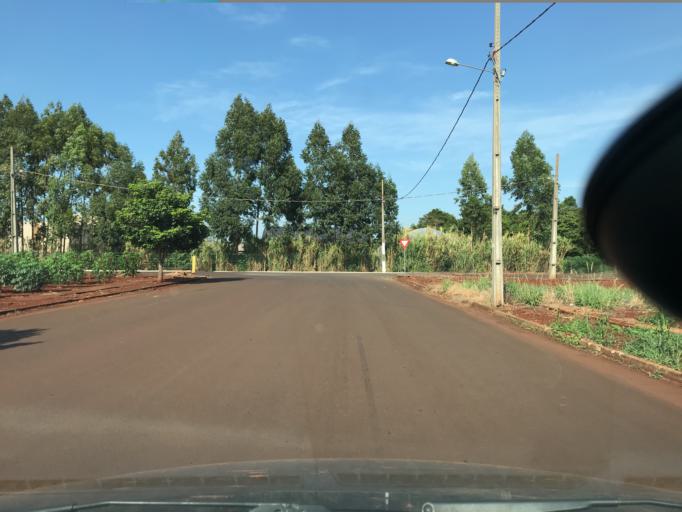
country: BR
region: Parana
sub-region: Palotina
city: Palotina
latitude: -24.2932
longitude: -53.8399
